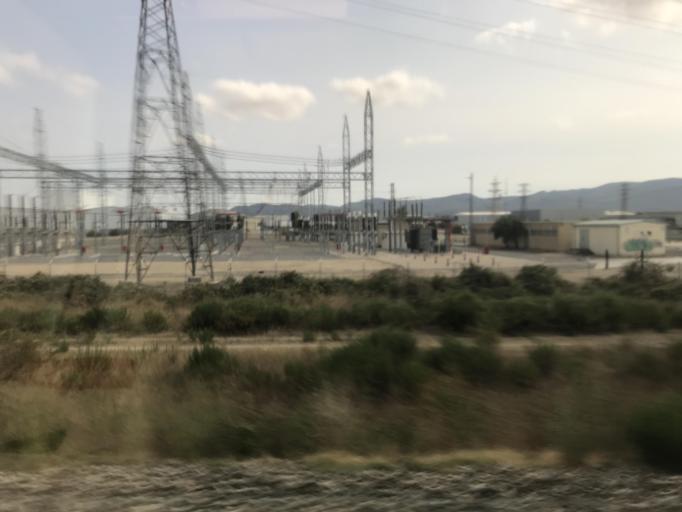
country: ES
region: Castille and Leon
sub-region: Provincia de Burgos
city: Miranda de Ebro
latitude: 42.6969
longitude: -2.9220
